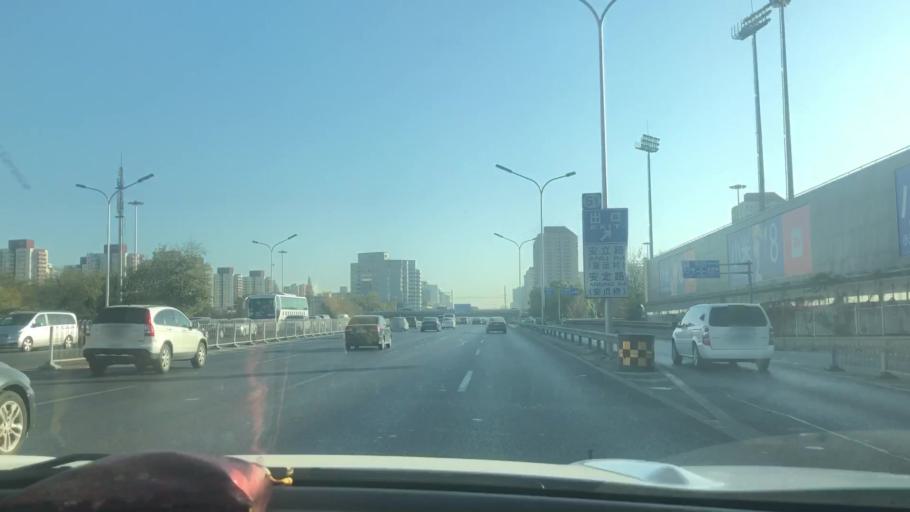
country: CN
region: Beijing
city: Datun
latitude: 39.9870
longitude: 116.3979
